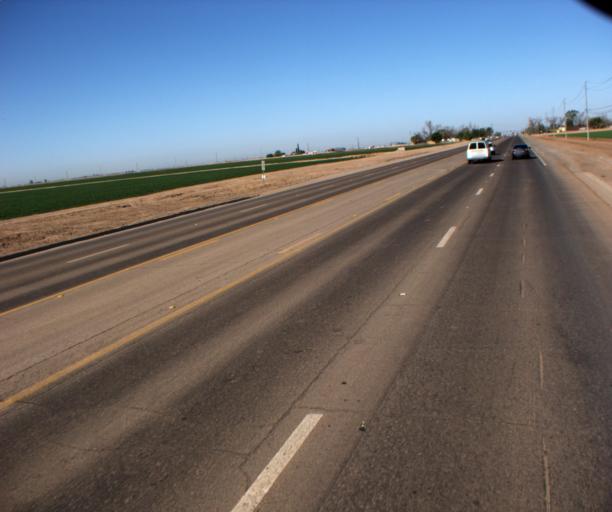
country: US
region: Arizona
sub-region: Yuma County
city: Somerton
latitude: 32.5968
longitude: -114.7272
